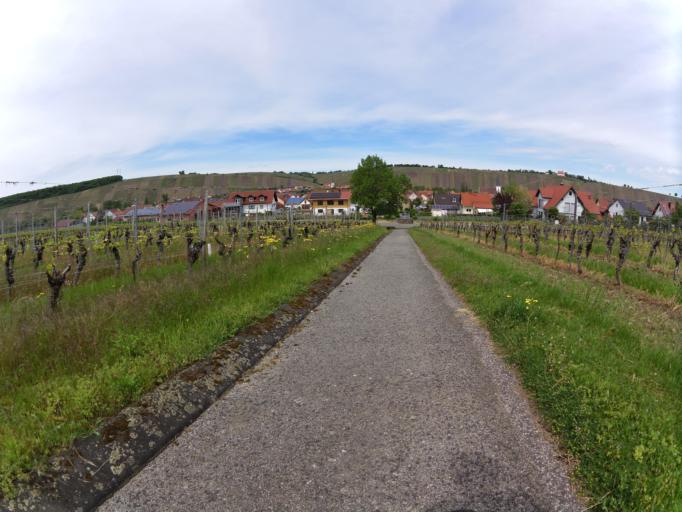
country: DE
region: Bavaria
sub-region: Regierungsbezirk Unterfranken
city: Nordheim
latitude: 49.8557
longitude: 10.1851
